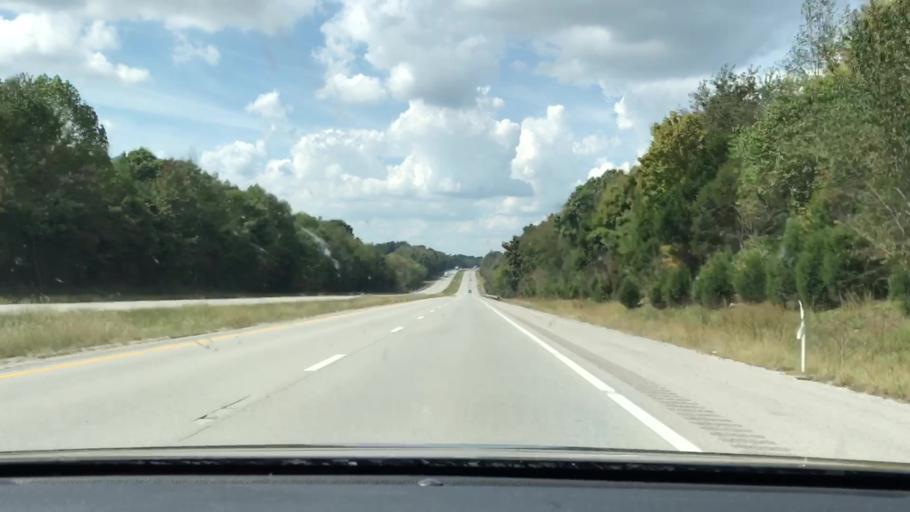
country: US
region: Kentucky
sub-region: Barren County
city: Glasgow
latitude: 37.0080
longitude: -86.0115
